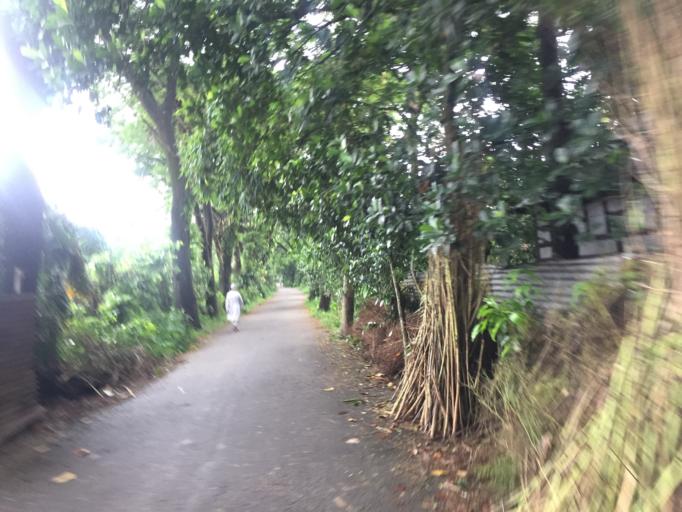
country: BD
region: Dhaka
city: Narayanganj
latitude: 23.5382
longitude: 90.4718
